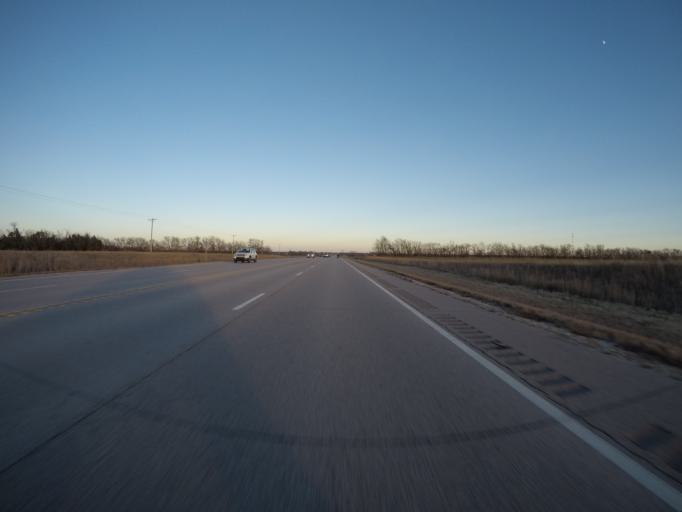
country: US
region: Kansas
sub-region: Marion County
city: Peabody
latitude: 38.1746
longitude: -97.1463
